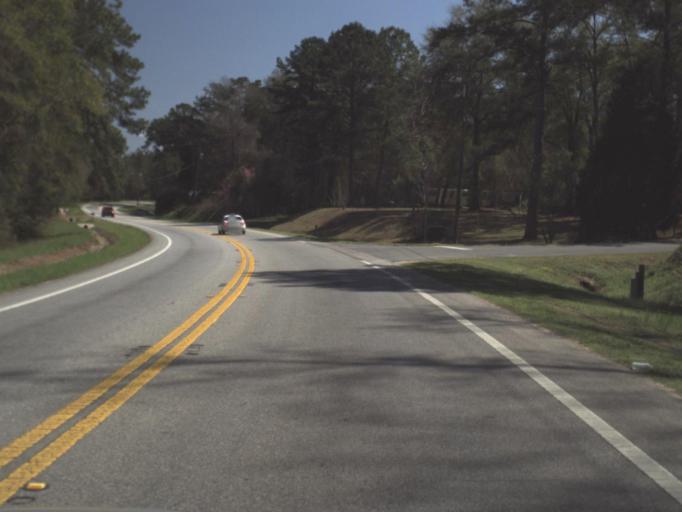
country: US
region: Florida
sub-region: Gadsden County
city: Quincy
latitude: 30.6092
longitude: -84.5880
